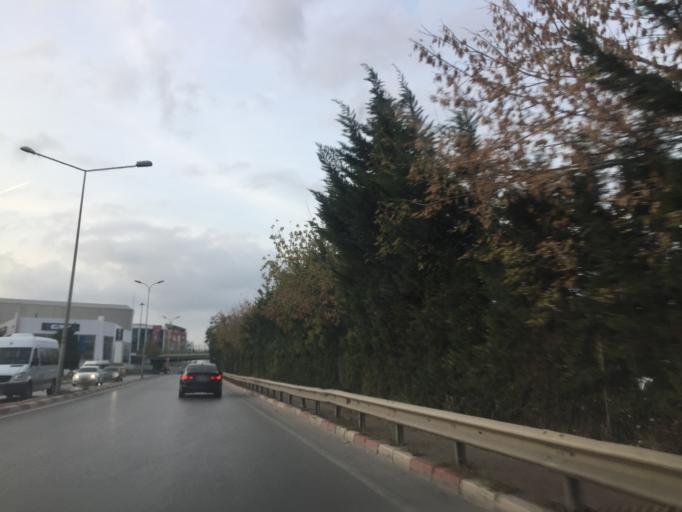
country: TR
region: Istanbul
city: Sultanbeyli
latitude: 40.9644
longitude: 29.2750
